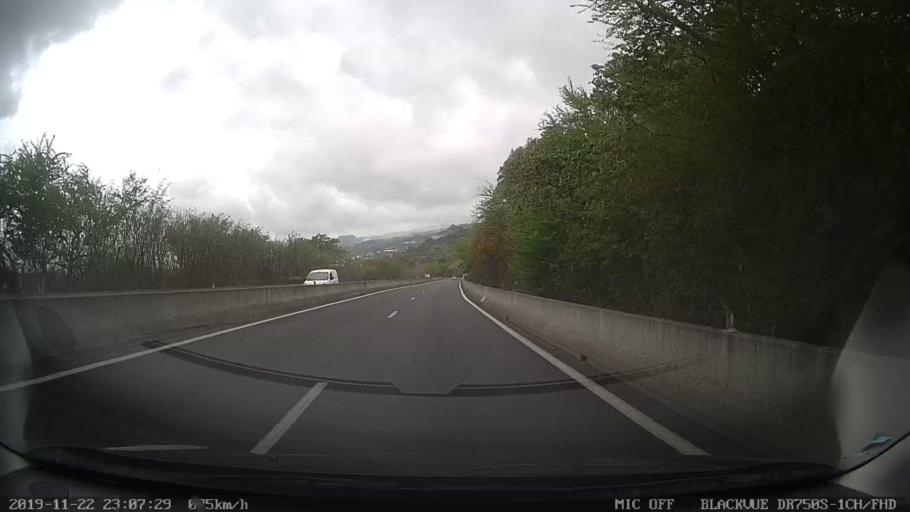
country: RE
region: Reunion
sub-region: Reunion
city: Saint-Denis
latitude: -20.8800
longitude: 55.4384
